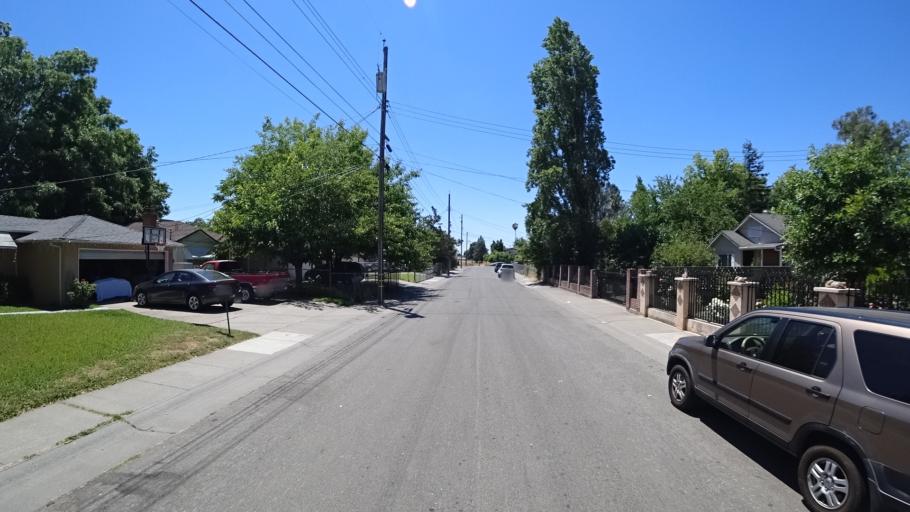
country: US
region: California
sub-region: Sacramento County
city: Parkway
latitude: 38.5297
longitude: -121.4629
